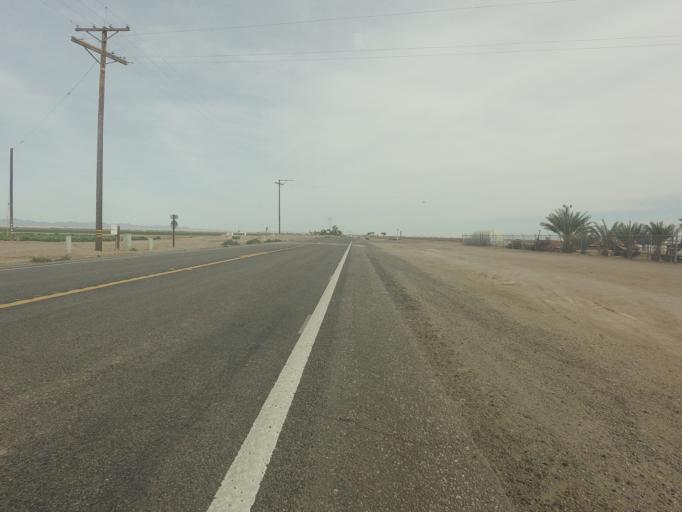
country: US
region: California
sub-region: Imperial County
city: Brawley
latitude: 32.9746
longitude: -115.3727
